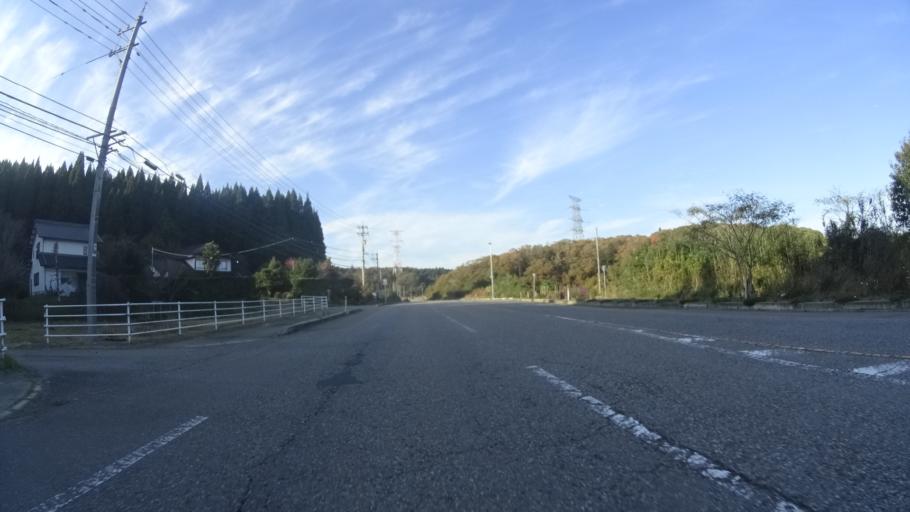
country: JP
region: Ishikawa
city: Hakui
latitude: 37.0438
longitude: 136.7762
